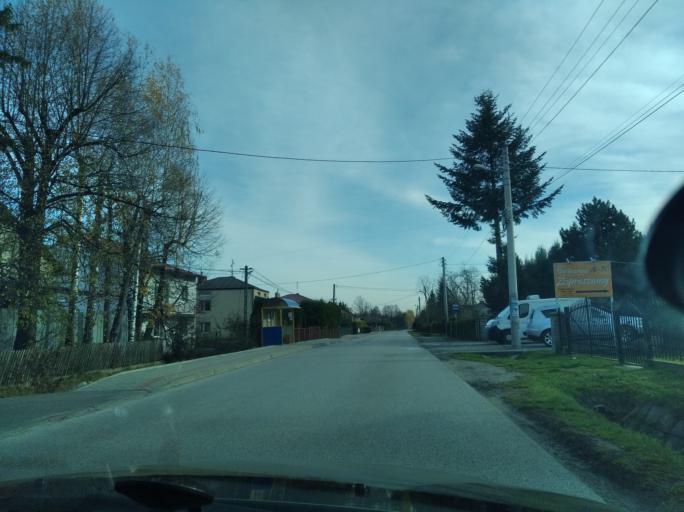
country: PL
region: Subcarpathian Voivodeship
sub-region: Powiat lancucki
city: Kraczkowa
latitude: 50.0369
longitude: 22.1399
